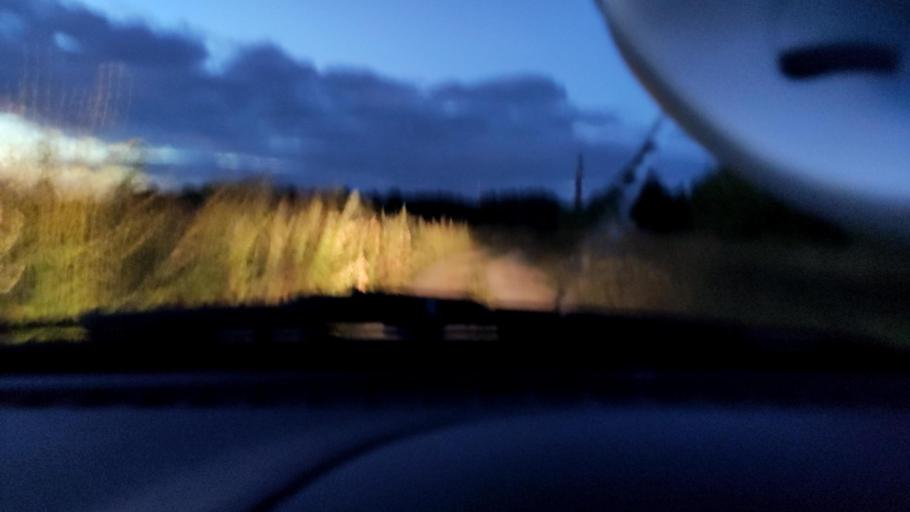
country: RU
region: Perm
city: Froly
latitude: 57.9443
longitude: 56.2534
